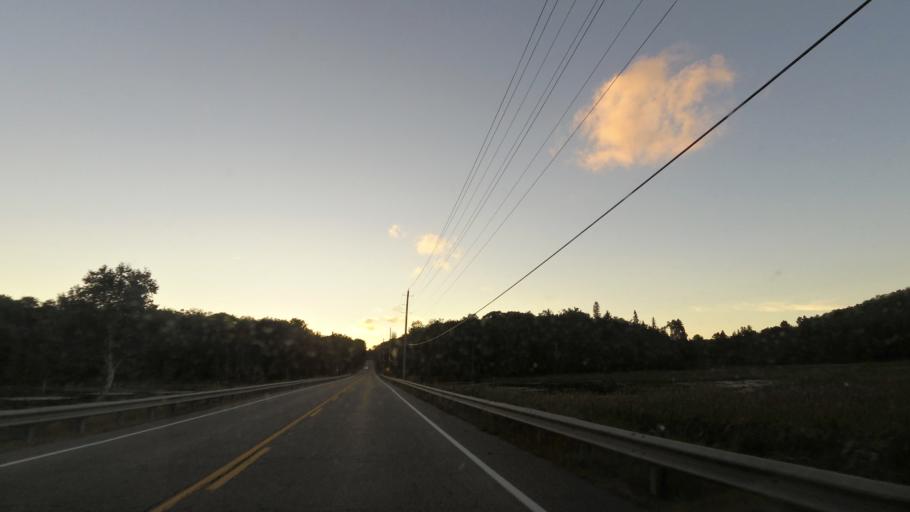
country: CA
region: Ontario
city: Bancroft
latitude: 45.0263
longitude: -78.3844
